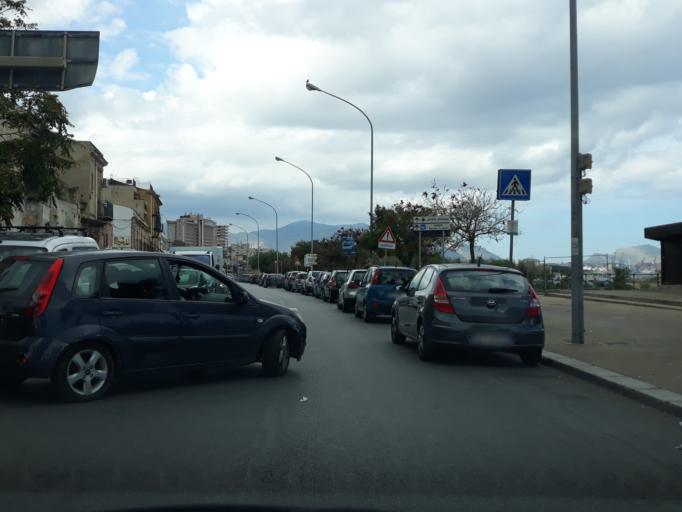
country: IT
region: Sicily
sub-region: Palermo
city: Ciaculli
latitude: 38.1056
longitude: 13.3883
